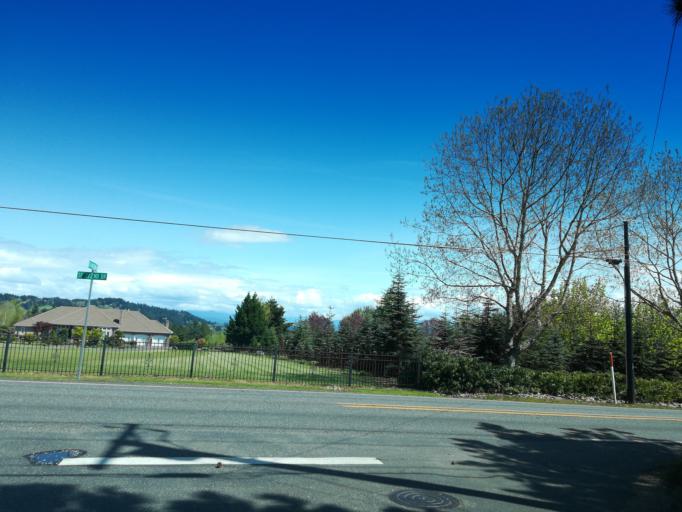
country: US
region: Oregon
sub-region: Clackamas County
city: Damascus
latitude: 45.4278
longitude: -122.4345
